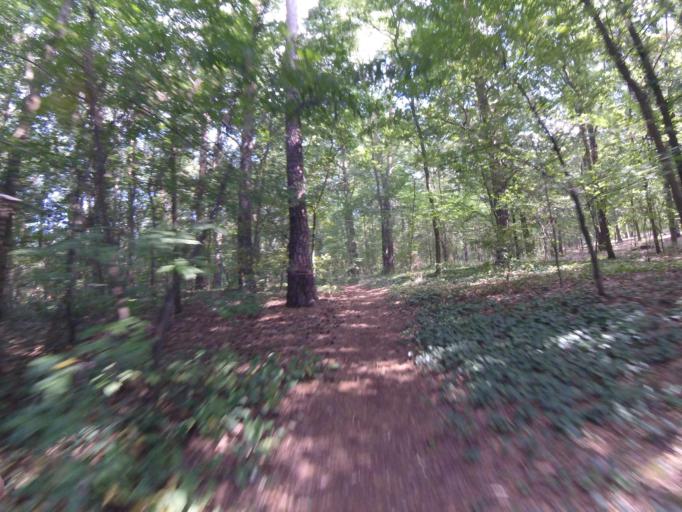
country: DE
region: Brandenburg
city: Konigs Wusterhausen
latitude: 52.2839
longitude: 13.6590
